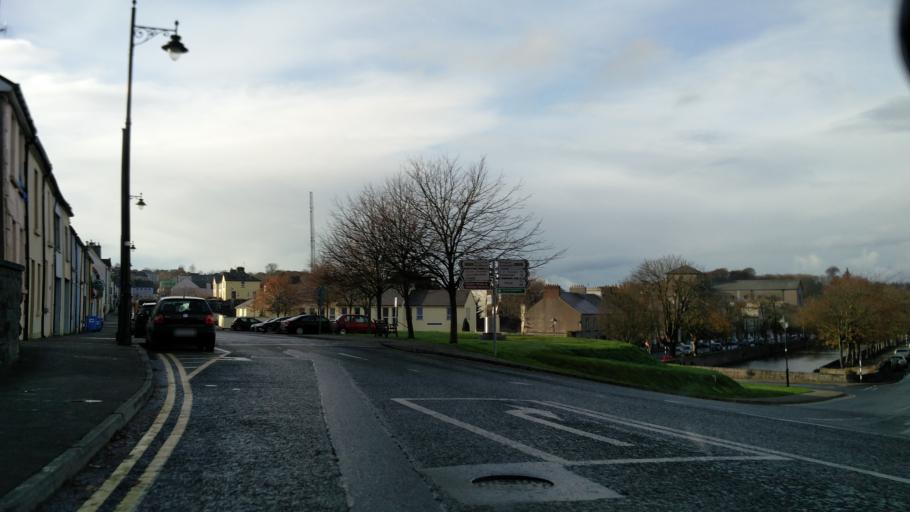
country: IE
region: Connaught
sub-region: Maigh Eo
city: Westport
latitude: 53.7992
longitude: -9.5176
